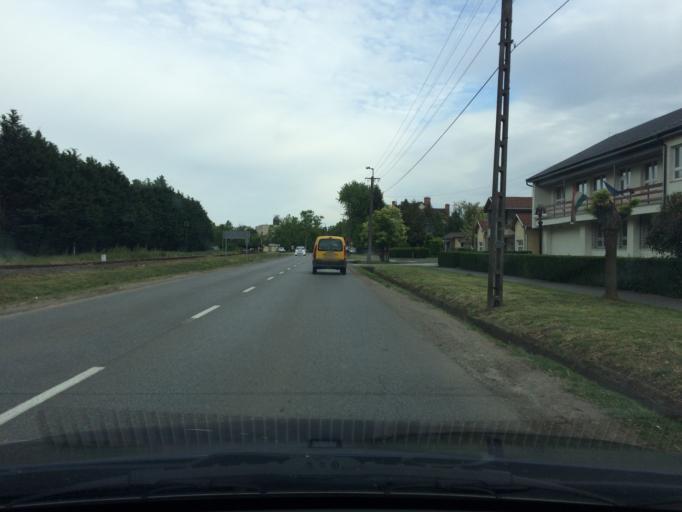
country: HU
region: Szabolcs-Szatmar-Bereg
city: Tiszavasvari
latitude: 47.9498
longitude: 21.3697
